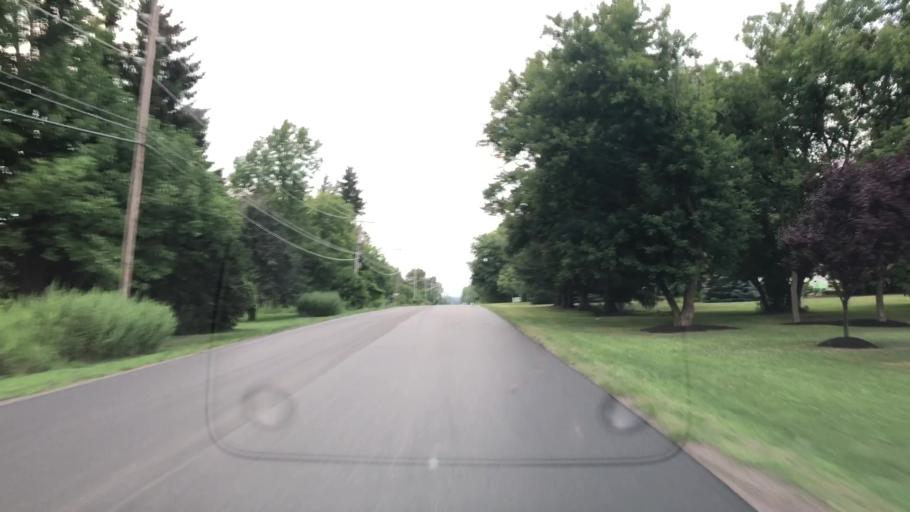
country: US
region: New York
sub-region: Erie County
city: Elma Center
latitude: 42.8157
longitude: -78.6059
